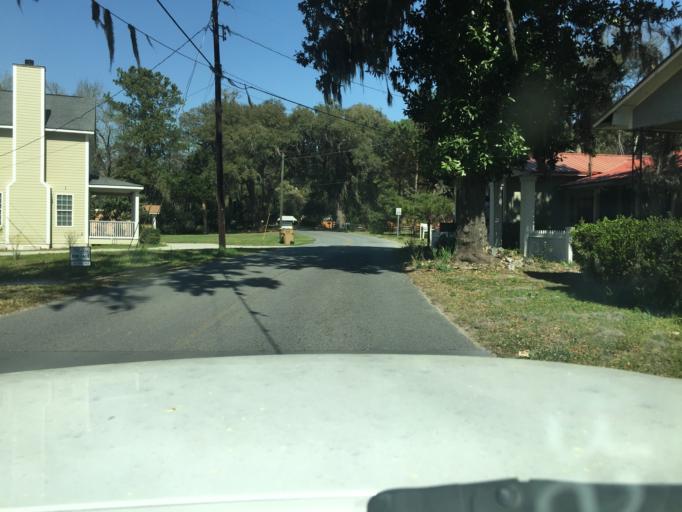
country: US
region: Georgia
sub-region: Chatham County
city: Thunderbolt
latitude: 32.0411
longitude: -81.0515
